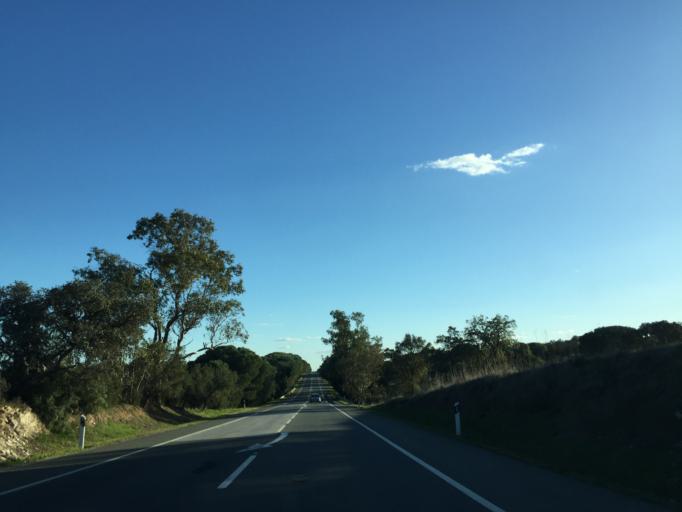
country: PT
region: Setubal
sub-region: Grandola
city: Grandola
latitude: 38.0899
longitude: -8.4181
